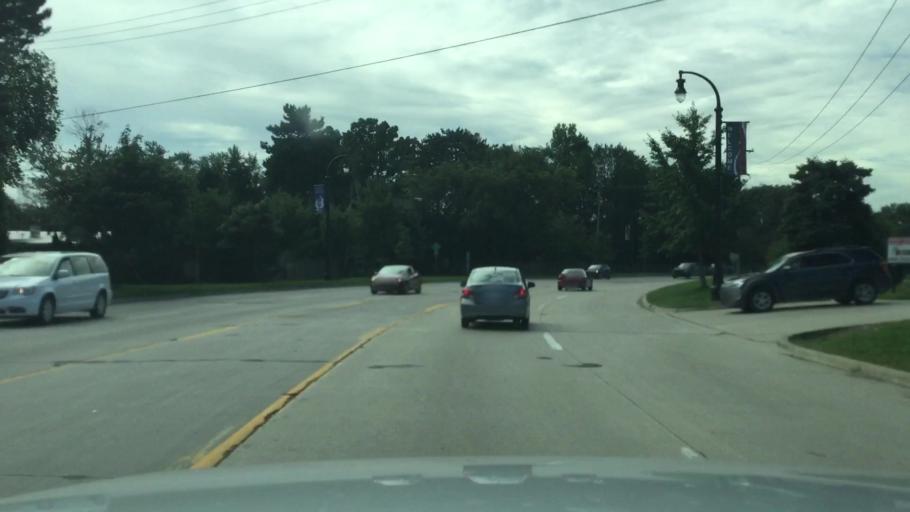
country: US
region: Michigan
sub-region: Wayne County
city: Belleville
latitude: 42.2158
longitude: -83.4853
